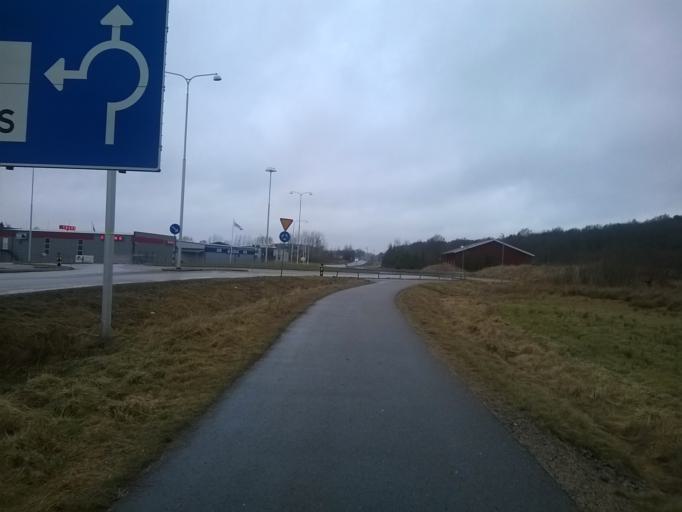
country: SE
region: Vaestra Goetaland
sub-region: Kungalvs Kommun
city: Kungalv
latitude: 57.8907
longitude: 11.9448
